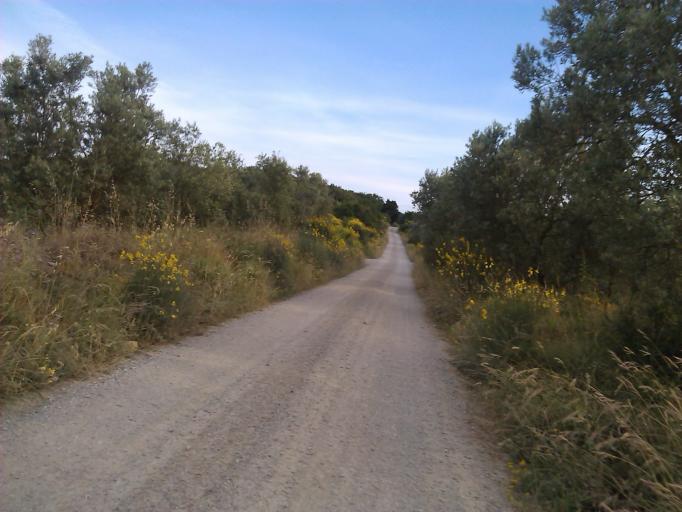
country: IT
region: Tuscany
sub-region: Province of Arezzo
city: Ponticino
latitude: 43.4651
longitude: 11.7293
